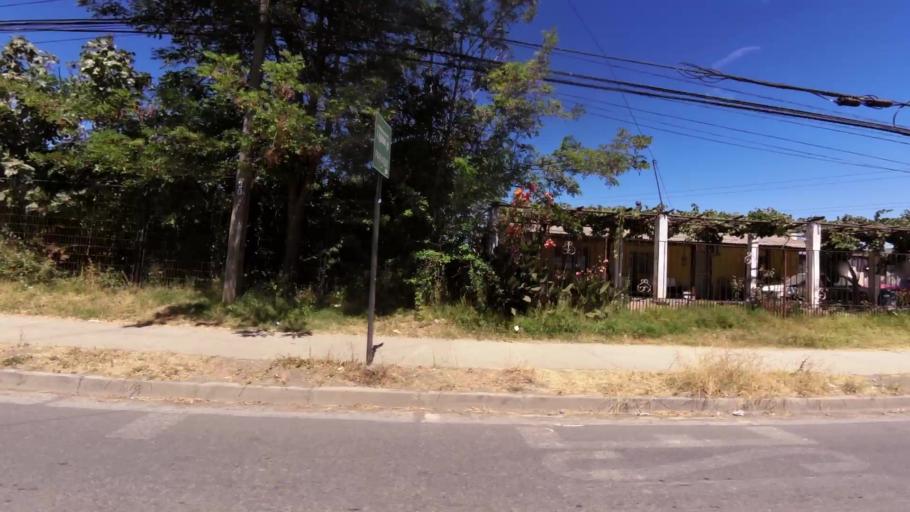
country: CL
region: O'Higgins
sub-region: Provincia de Cachapoal
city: Rancagua
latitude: -34.1459
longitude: -70.7255
